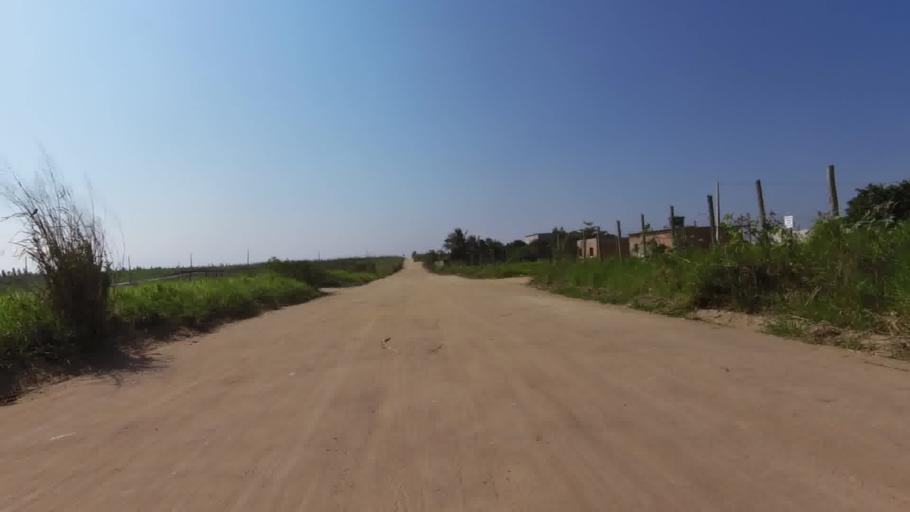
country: BR
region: Espirito Santo
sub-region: Marataizes
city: Marataizes
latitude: -21.0413
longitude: -40.8431
